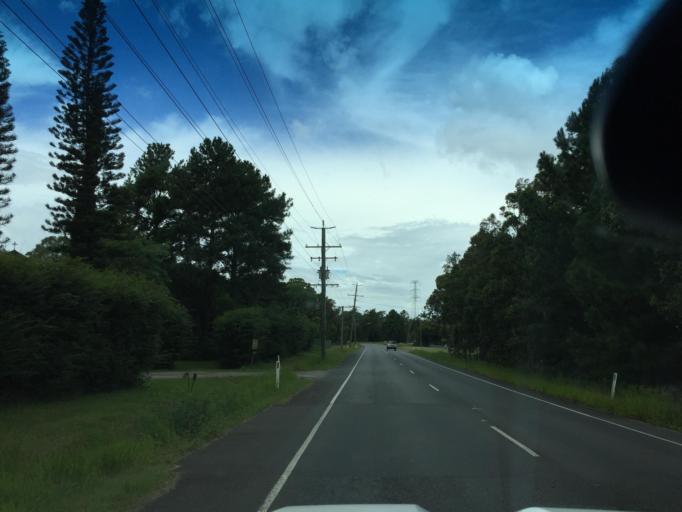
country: AU
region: Queensland
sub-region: Moreton Bay
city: Caboolture
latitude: -27.0664
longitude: 152.9134
